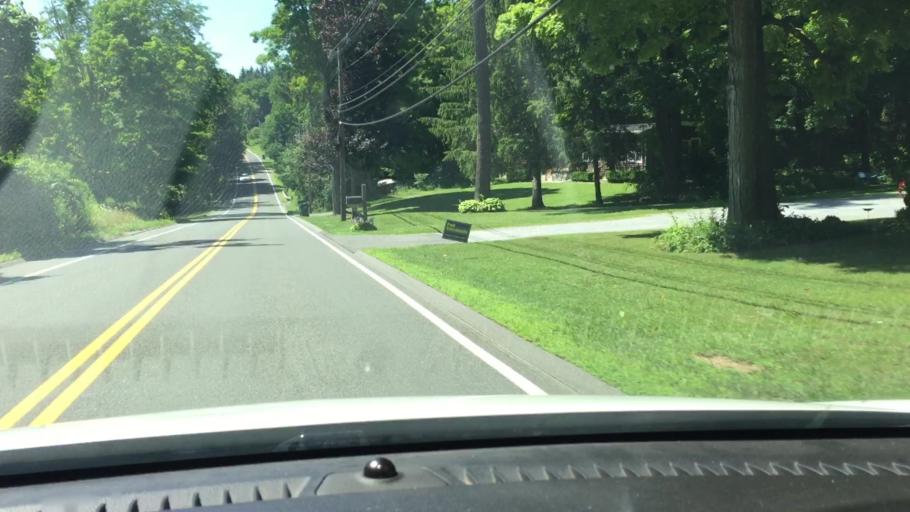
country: US
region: Massachusetts
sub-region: Berkshire County
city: Lenox
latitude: 42.3664
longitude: -73.2596
